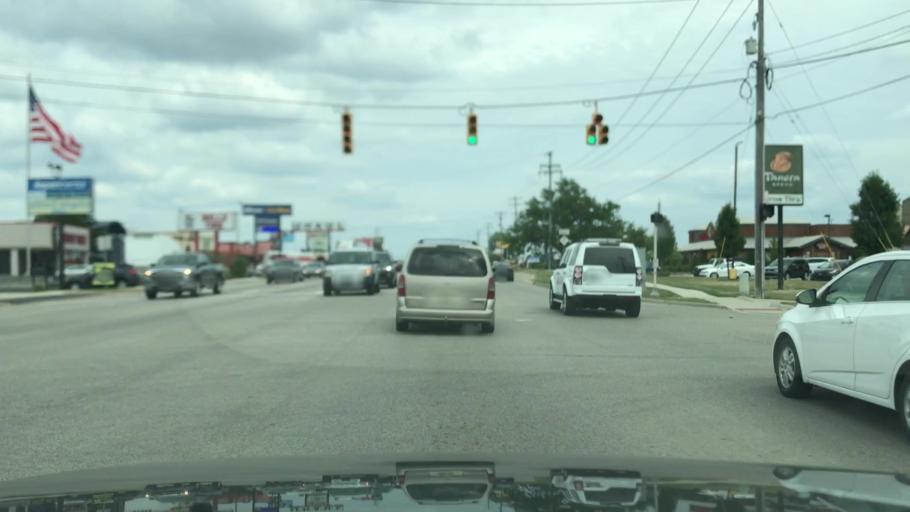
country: US
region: Michigan
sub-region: Kent County
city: East Grand Rapids
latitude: 42.9125
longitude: -85.5752
